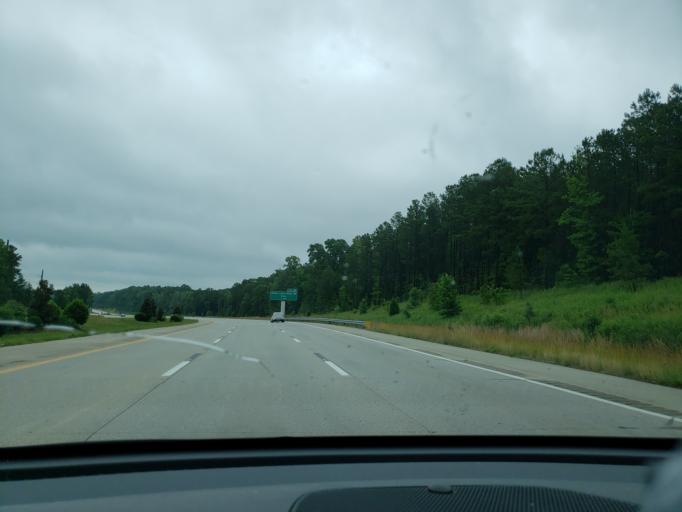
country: US
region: North Carolina
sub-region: Wake County
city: Green Level
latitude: 35.7673
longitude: -78.8866
